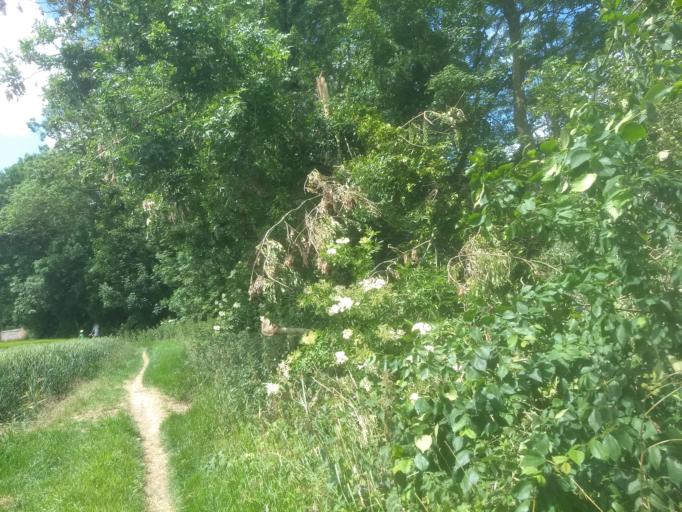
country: FR
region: Nord-Pas-de-Calais
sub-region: Departement du Pas-de-Calais
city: Agny
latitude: 50.2538
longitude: 2.7383
